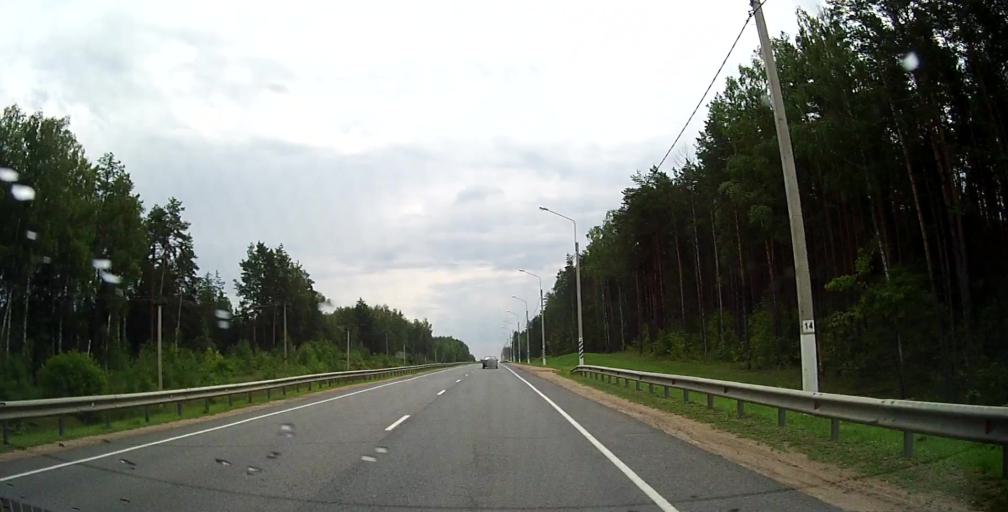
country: RU
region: Smolensk
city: Katyn'
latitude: 54.7730
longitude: 31.7734
